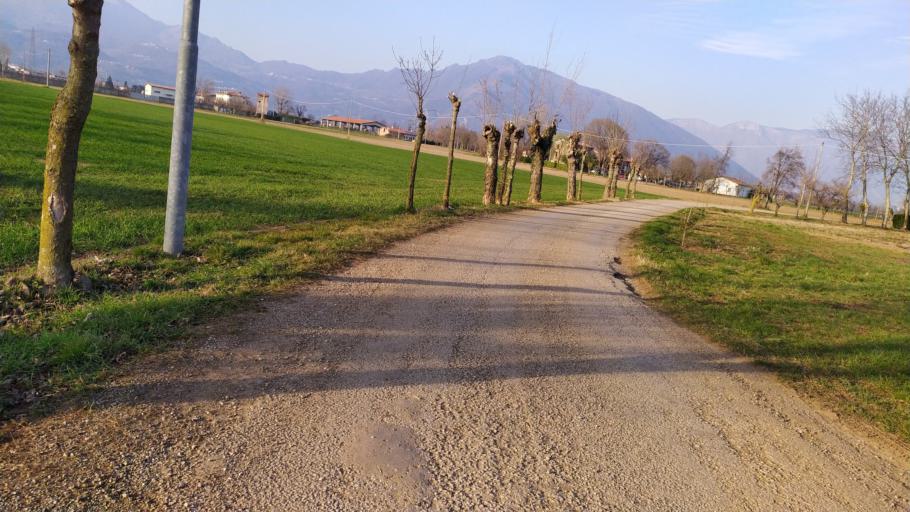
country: IT
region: Veneto
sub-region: Provincia di Vicenza
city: San Vito di Leguzzano
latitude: 45.6886
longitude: 11.3805
